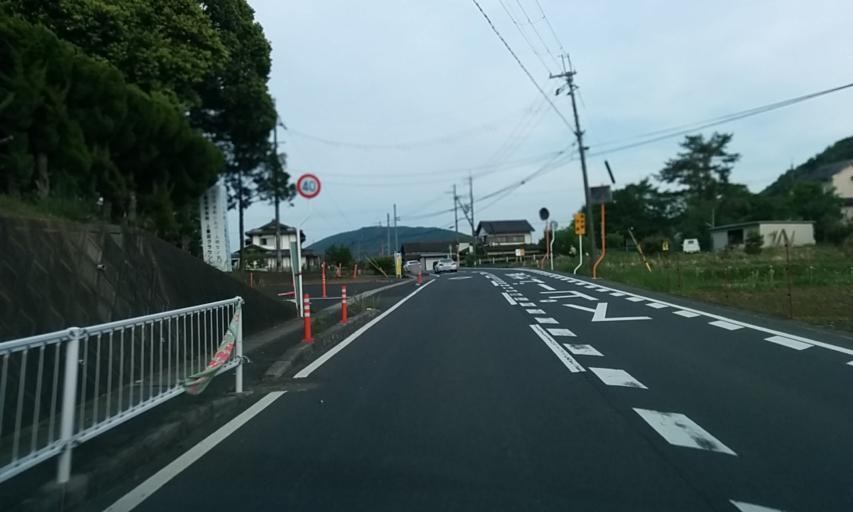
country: JP
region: Kyoto
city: Ayabe
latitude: 35.1653
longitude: 135.3994
